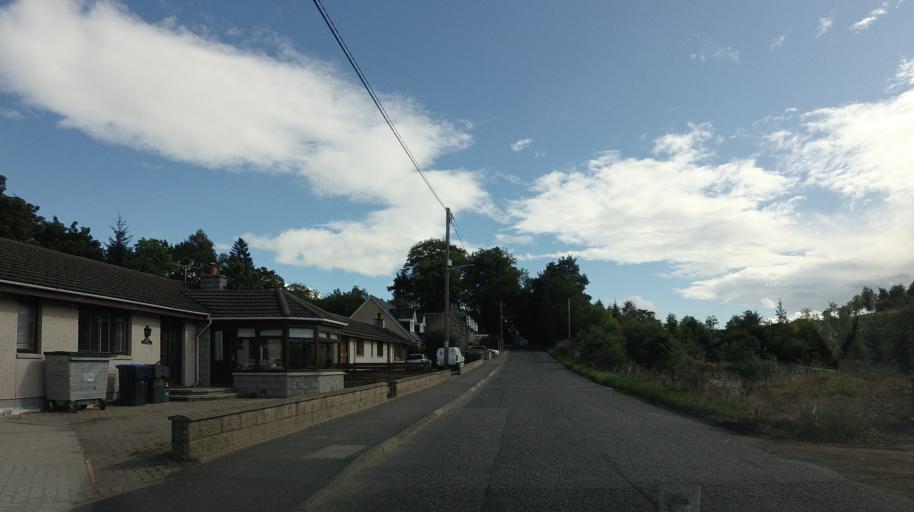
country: GB
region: Scotland
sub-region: Aberdeenshire
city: Torphins
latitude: 57.1279
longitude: -2.6833
